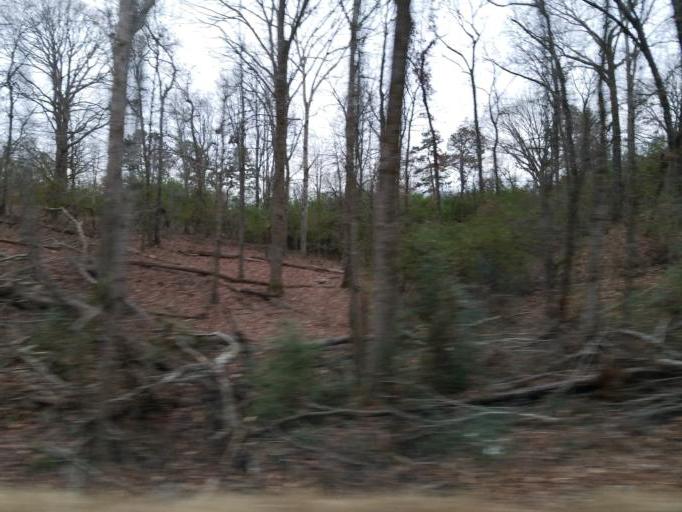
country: US
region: Georgia
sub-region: Dawson County
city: Dawsonville
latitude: 34.4149
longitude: -84.0290
